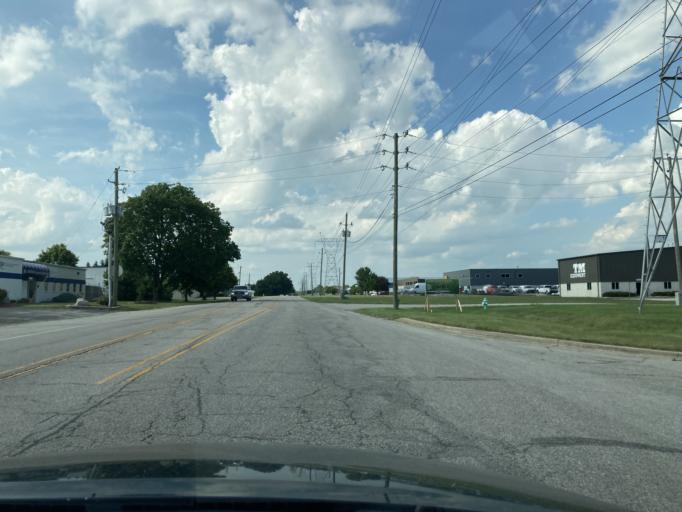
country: US
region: Indiana
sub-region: Marion County
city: Meridian Hills
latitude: 39.8733
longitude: -86.2316
